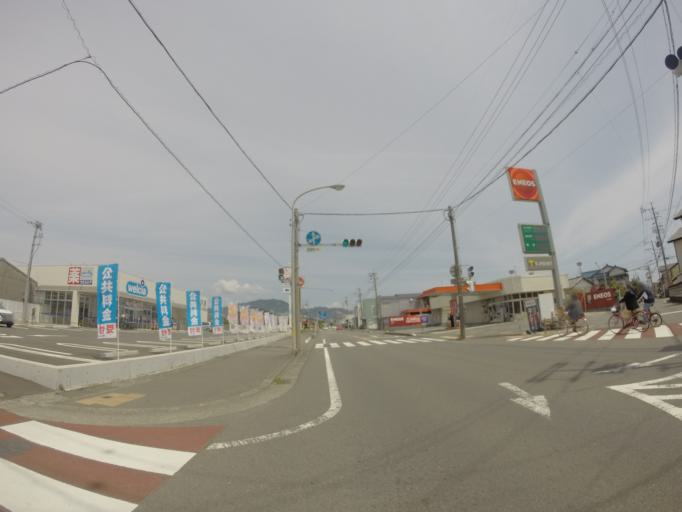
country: JP
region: Shizuoka
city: Yaizu
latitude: 34.8565
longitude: 138.3178
